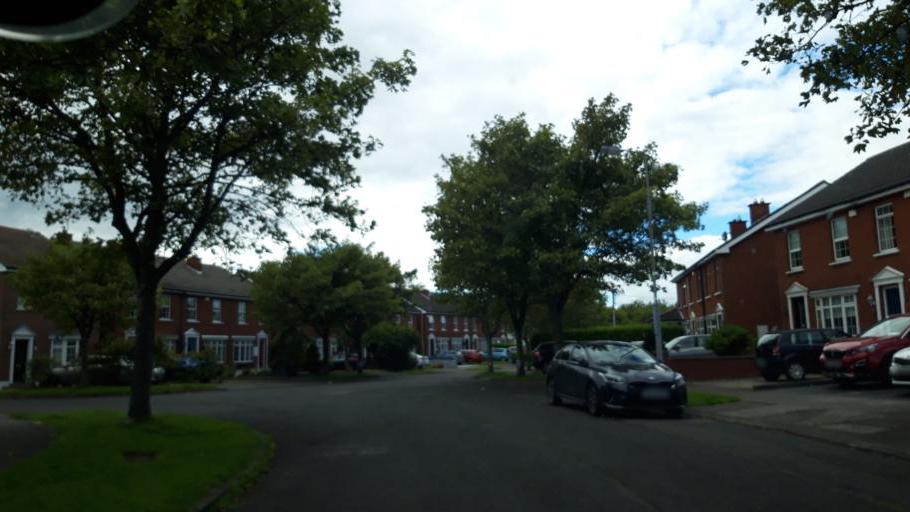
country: IE
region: Leinster
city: Dollymount
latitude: 53.3613
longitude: -6.1865
